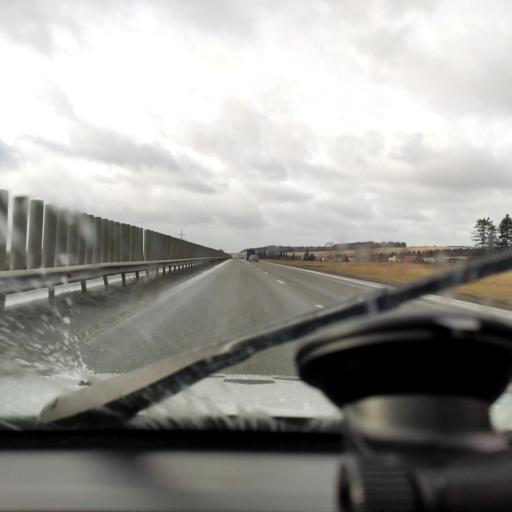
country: RU
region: Perm
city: Froly
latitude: 57.9339
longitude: 56.2554
